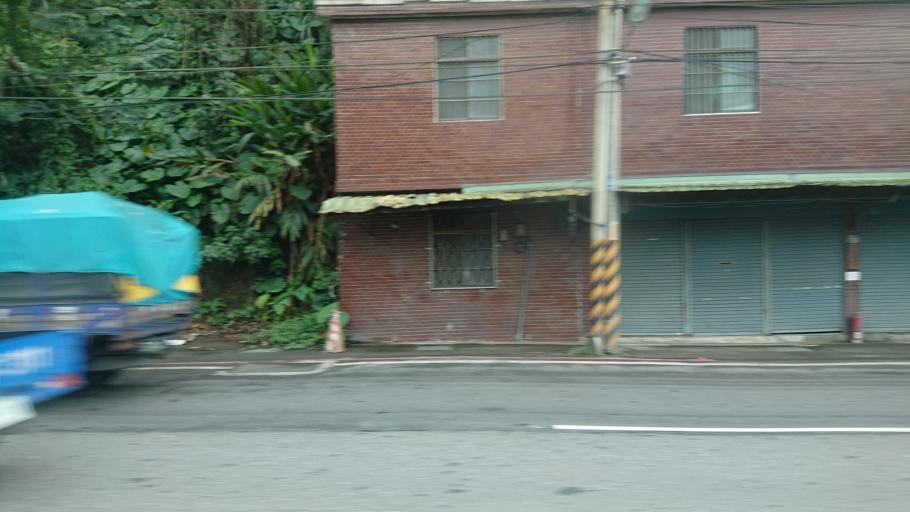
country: TW
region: Taipei
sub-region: Taipei
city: Banqiao
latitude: 24.9456
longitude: 121.4045
